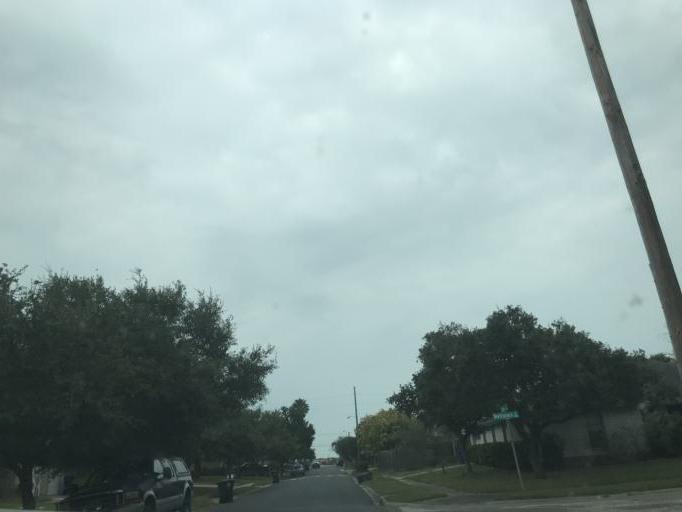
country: US
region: Texas
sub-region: Nueces County
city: Corpus Christi
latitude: 27.6739
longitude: -97.3486
